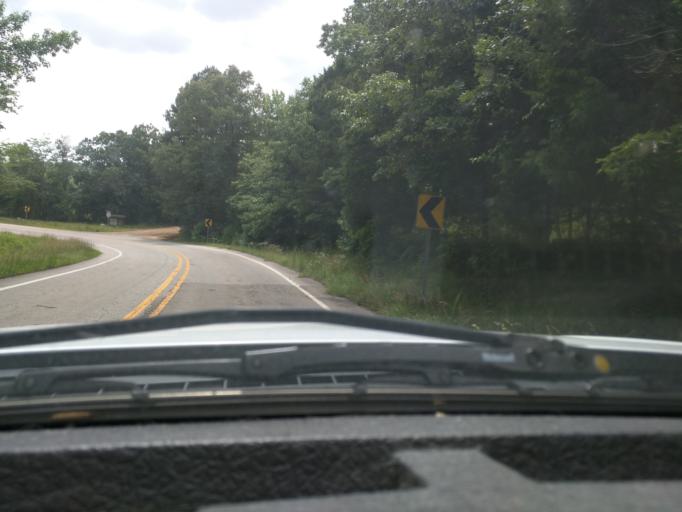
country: US
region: Arkansas
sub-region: Franklin County
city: Ozark
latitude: 35.6752
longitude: -93.8327
